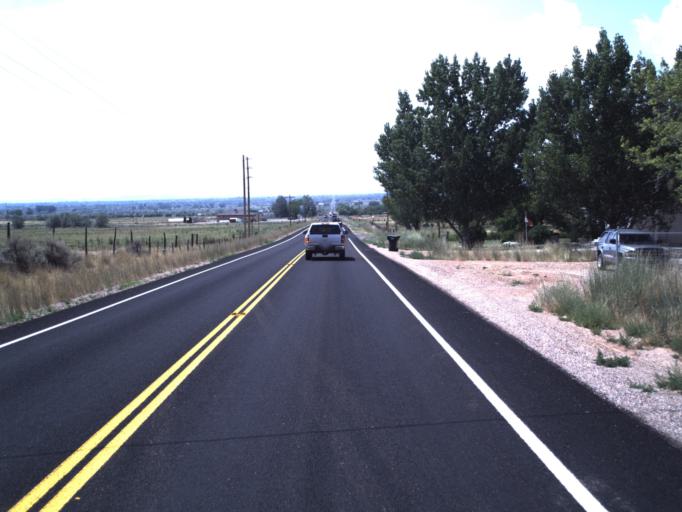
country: US
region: Utah
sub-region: Duchesne County
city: Roosevelt
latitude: 40.4037
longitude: -109.8156
